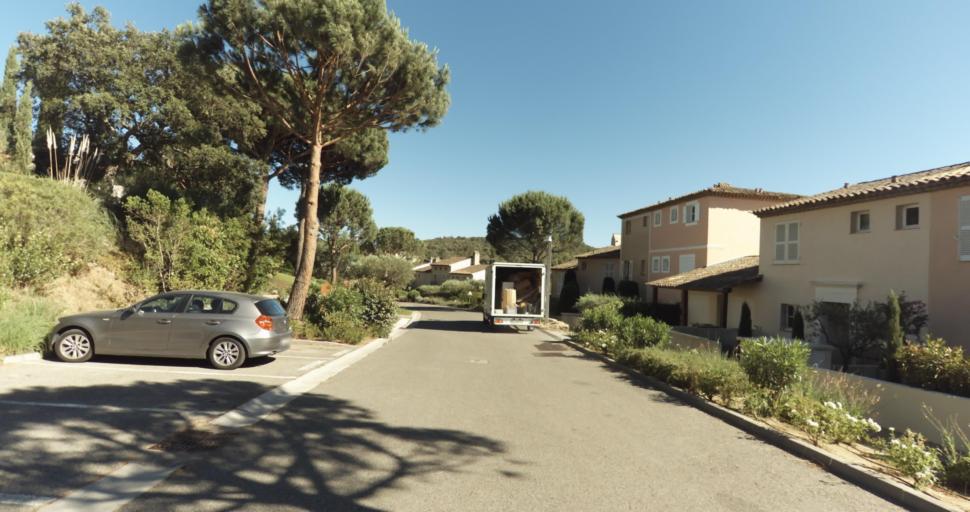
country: FR
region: Provence-Alpes-Cote d'Azur
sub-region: Departement du Var
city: Gassin
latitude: 43.2542
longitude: 6.6034
